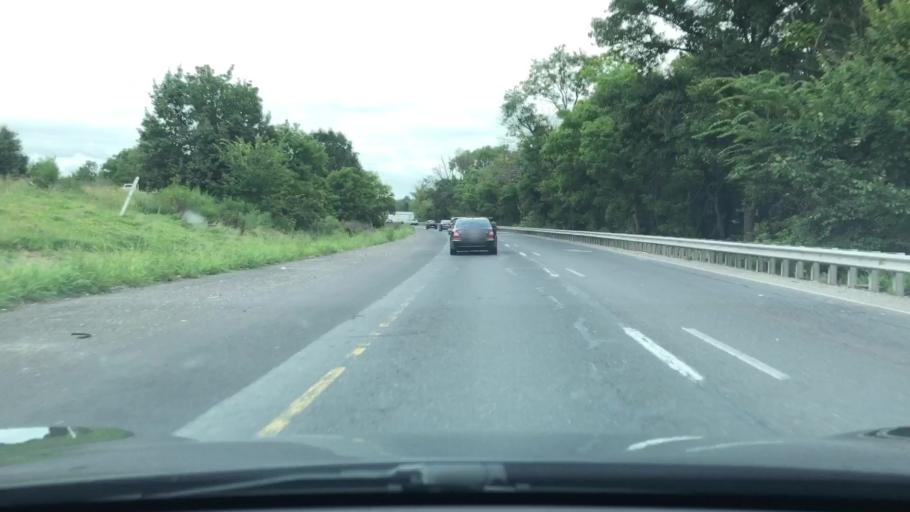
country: US
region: Pennsylvania
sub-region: Bucks County
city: Morrisville
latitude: 40.1975
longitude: -74.7925
